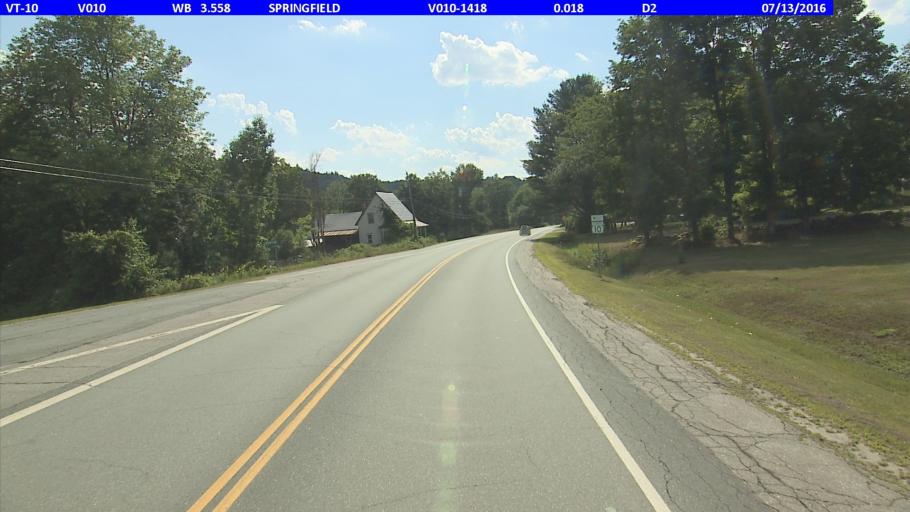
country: US
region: Vermont
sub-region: Windsor County
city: Springfield
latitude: 43.3351
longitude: -72.5461
